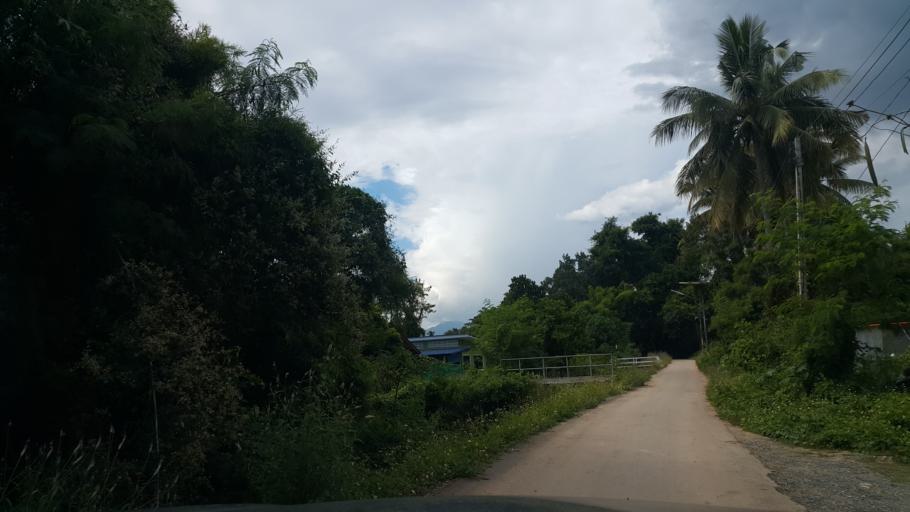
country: TH
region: Chiang Mai
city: Chiang Mai
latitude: 18.8317
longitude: 98.9987
